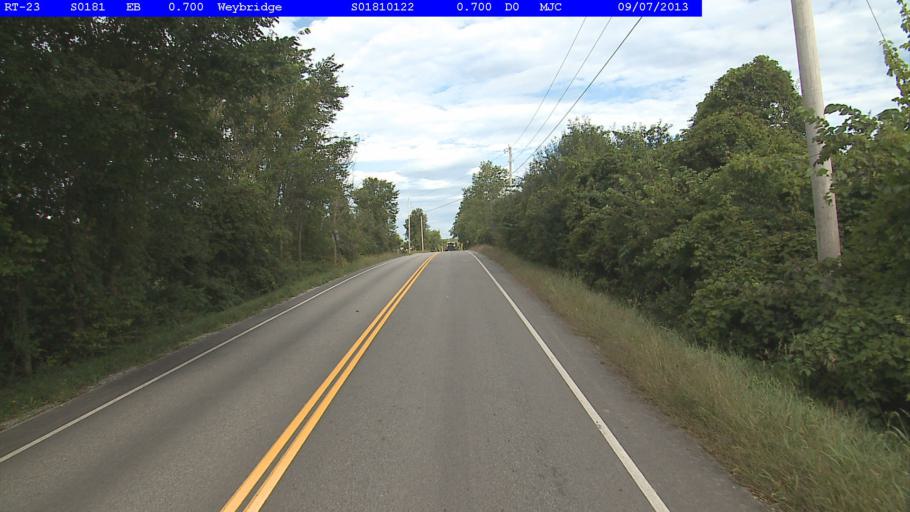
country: US
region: Vermont
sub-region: Addison County
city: Middlebury (village)
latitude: 44.0250
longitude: -73.1936
